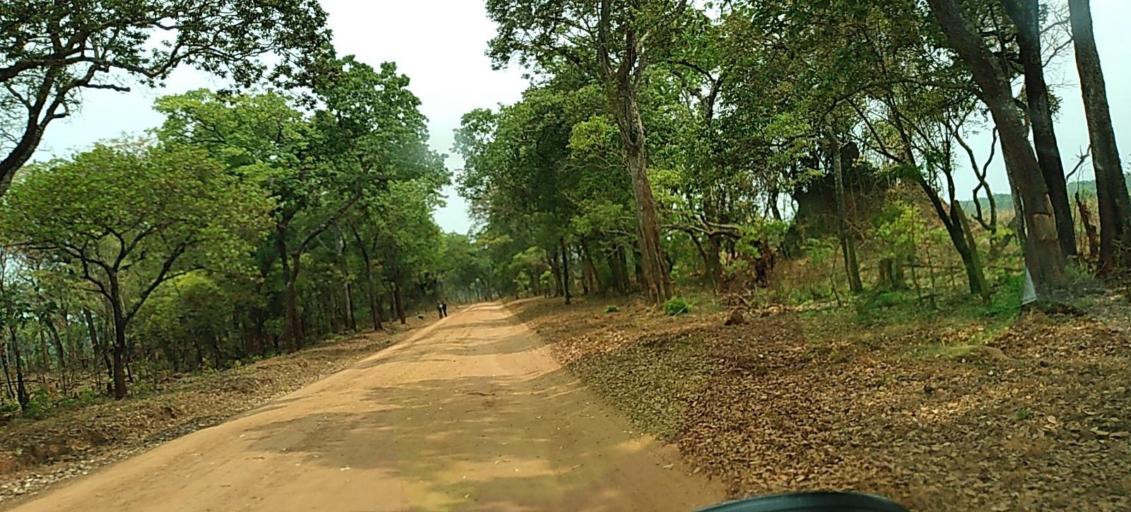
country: ZM
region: North-Western
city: Solwezi
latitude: -12.8143
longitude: 26.5365
